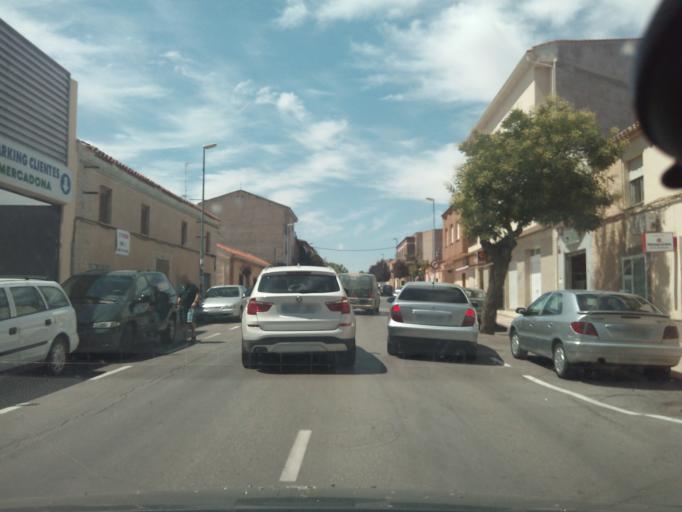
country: ES
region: Castille-La Mancha
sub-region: Province of Toledo
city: Villacanas
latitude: 39.6190
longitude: -3.3361
